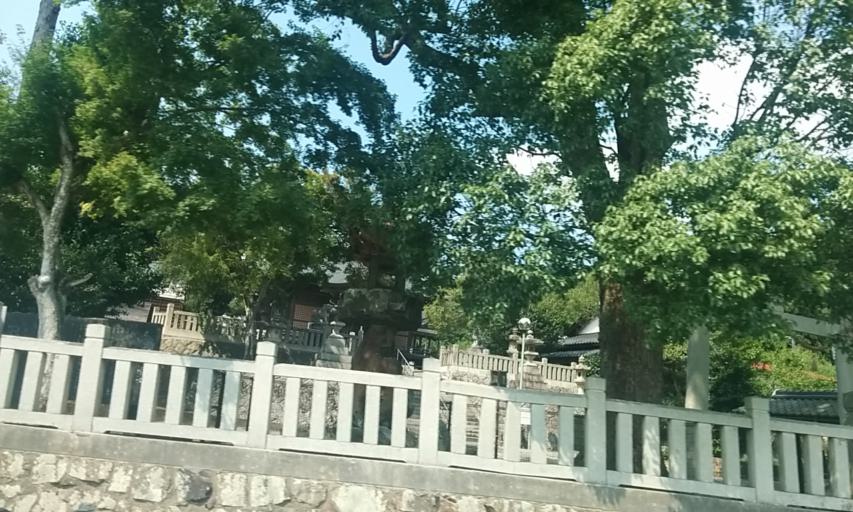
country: JP
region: Kyoto
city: Fukuchiyama
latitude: 35.3195
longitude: 135.1210
